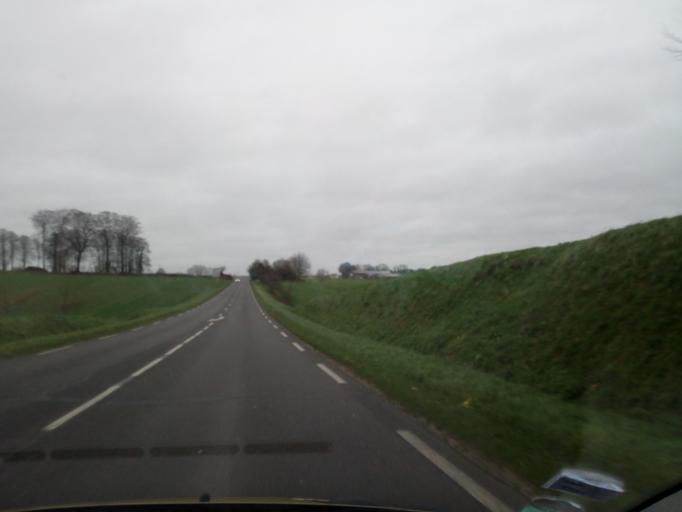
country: FR
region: Haute-Normandie
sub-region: Departement de la Seine-Maritime
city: Auzebosc
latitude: 49.5916
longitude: 0.7347
